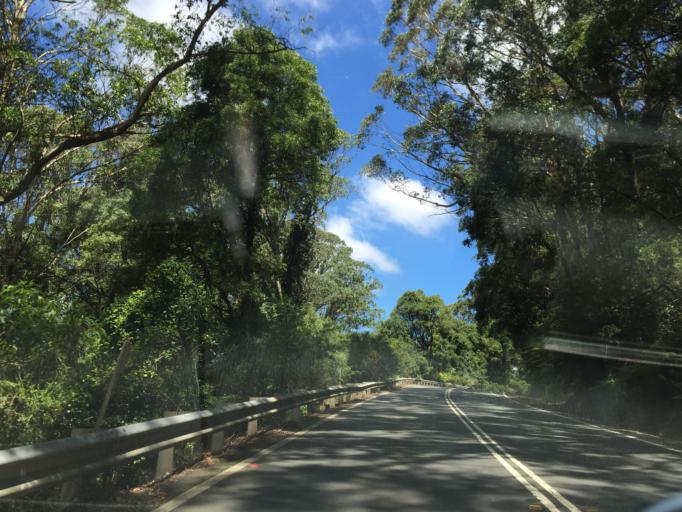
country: AU
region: New South Wales
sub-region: Blue Mountains Municipality
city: Blackheath
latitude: -33.5440
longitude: 150.4259
